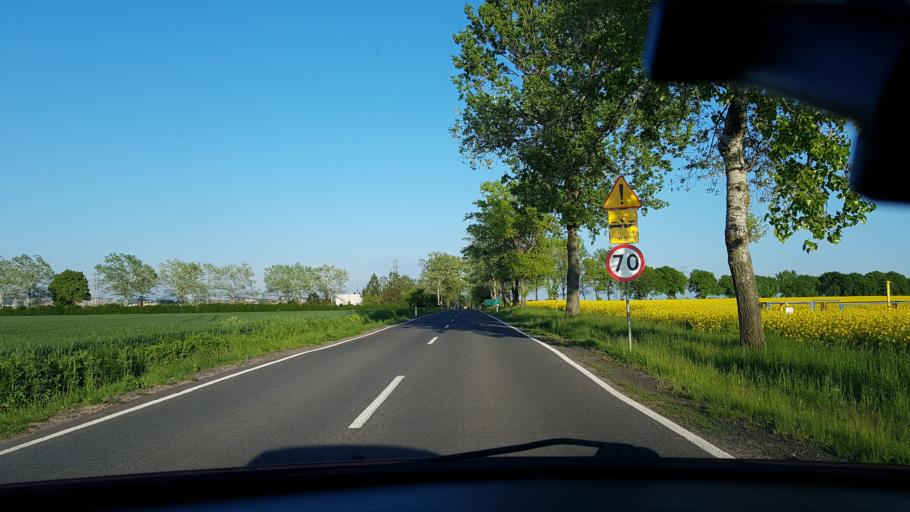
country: PL
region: Lower Silesian Voivodeship
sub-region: Powiat zabkowicki
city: Zabkowice Slaskie
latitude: 50.5945
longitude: 16.7832
